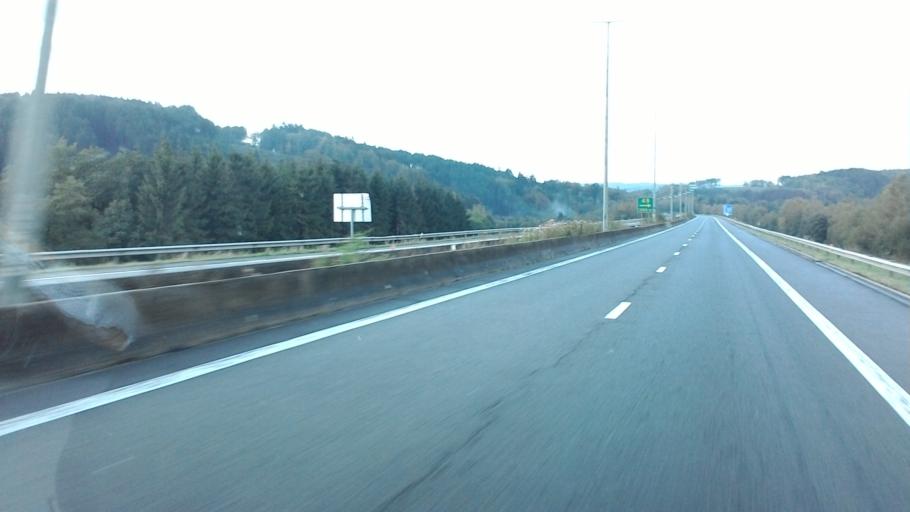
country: BE
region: Wallonia
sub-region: Province du Luxembourg
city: Manhay
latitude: 50.2929
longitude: 5.7260
